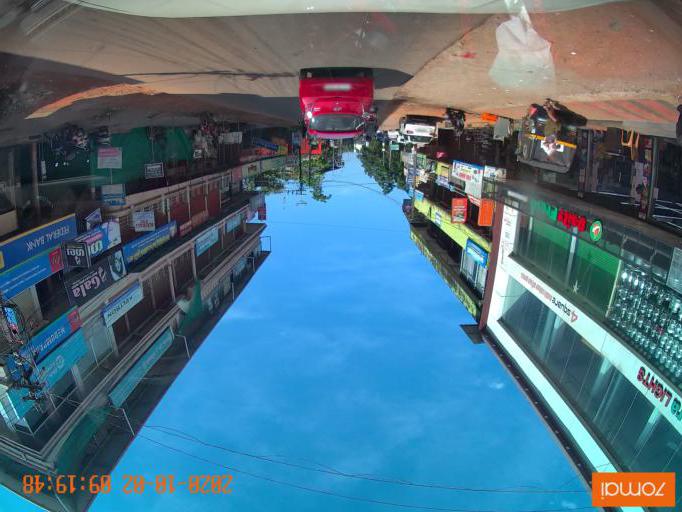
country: IN
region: Kerala
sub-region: Kozhikode
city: Naduvannur
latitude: 11.5644
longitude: 75.7563
